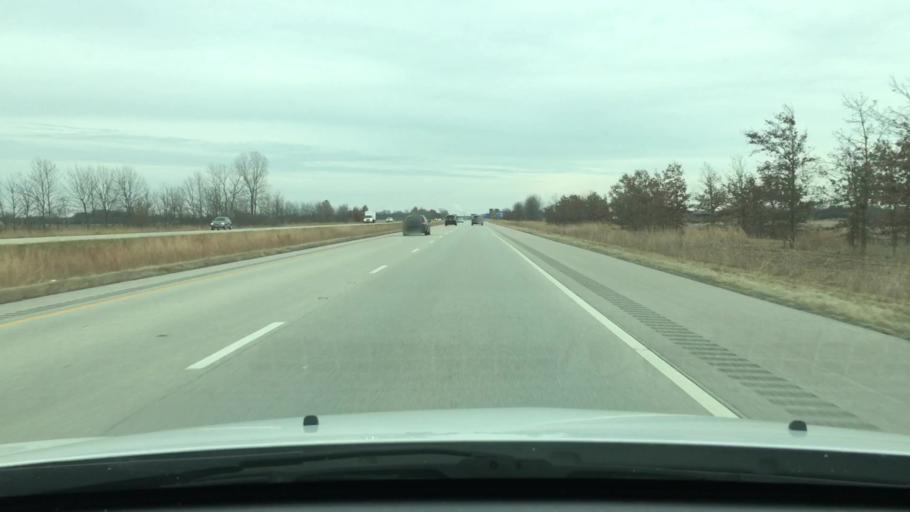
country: US
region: Illinois
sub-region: Sangamon County
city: Jerome
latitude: 39.7516
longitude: -89.7899
